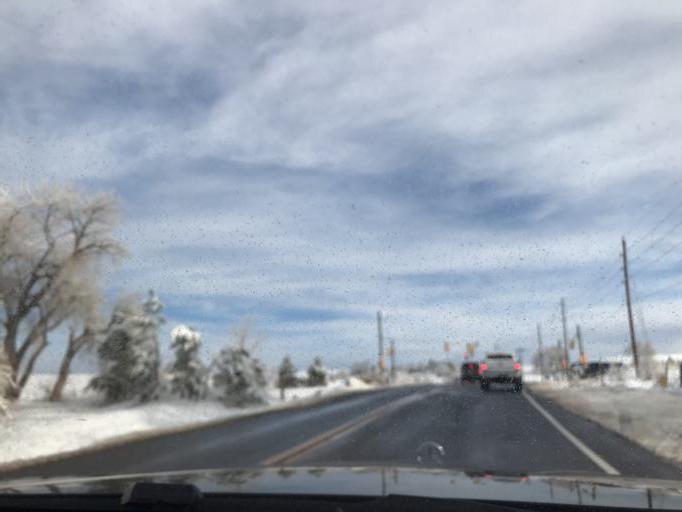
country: US
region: Colorado
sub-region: Jefferson County
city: Applewood
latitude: 39.8423
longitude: -105.1652
